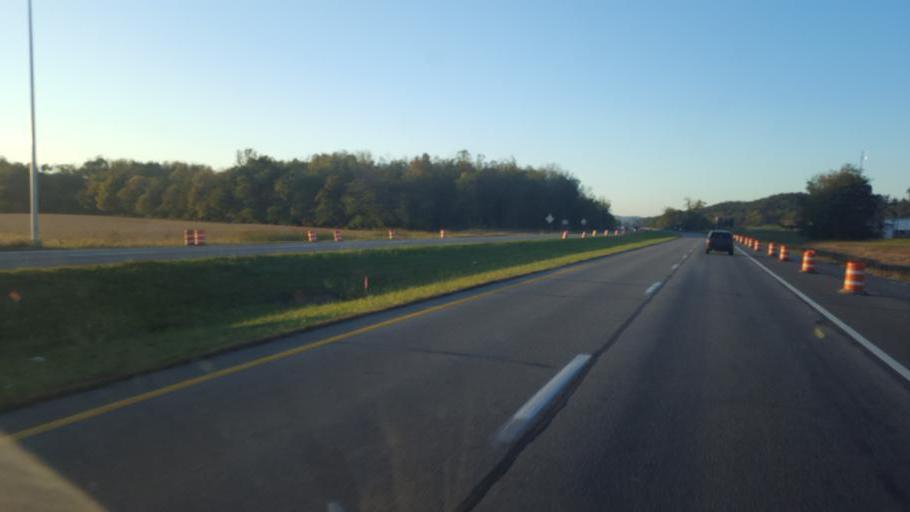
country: US
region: Ohio
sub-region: Scioto County
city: Lucasville
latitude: 38.8989
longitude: -83.0032
